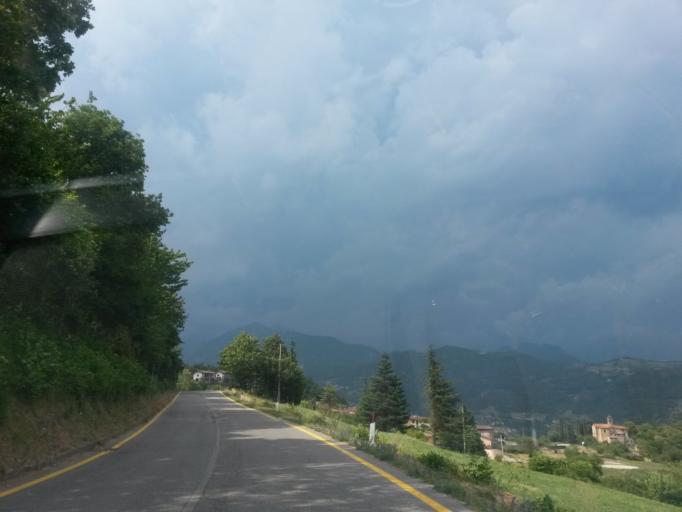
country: IT
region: Lombardy
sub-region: Provincia di Brescia
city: Gardola
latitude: 45.7493
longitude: 10.7309
